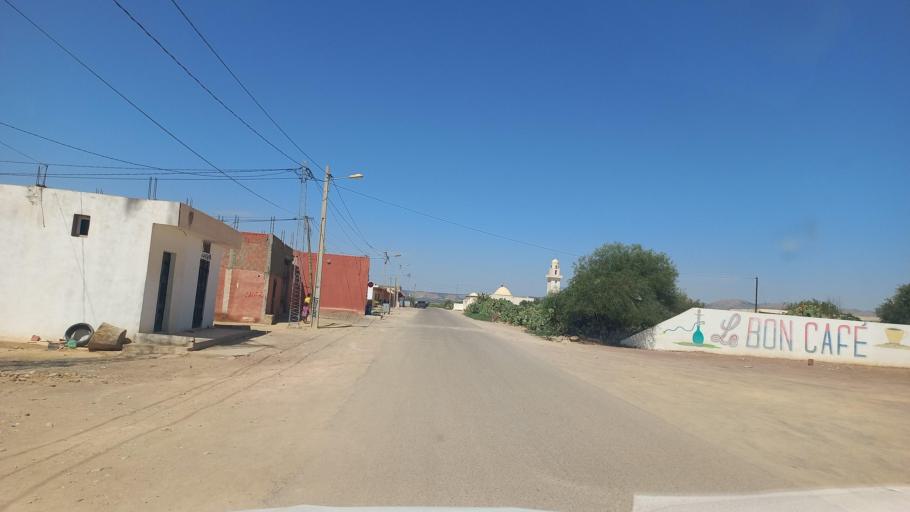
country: TN
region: Al Qasrayn
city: Sbiba
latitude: 35.3626
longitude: 9.0903
